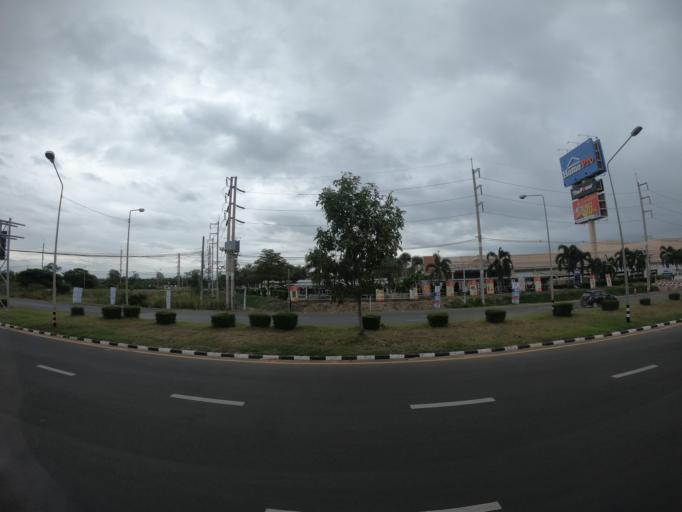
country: TH
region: Roi Et
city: Roi Et
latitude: 16.0623
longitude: 103.6190
